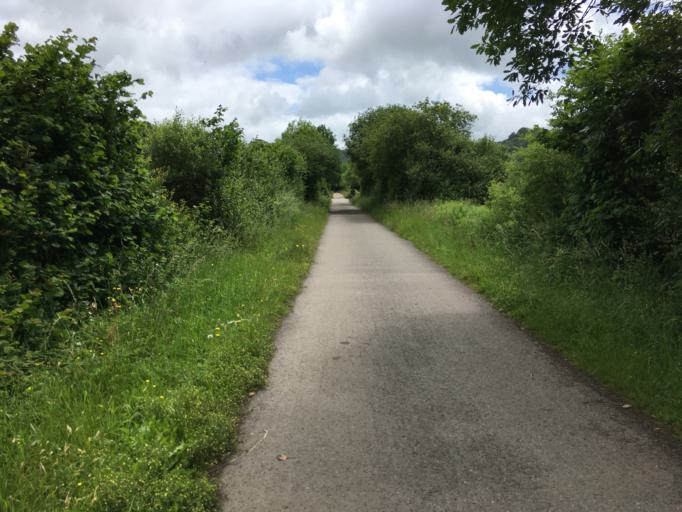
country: GB
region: England
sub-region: Cornwall
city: Wadebridge
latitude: 50.5054
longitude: -4.8170
